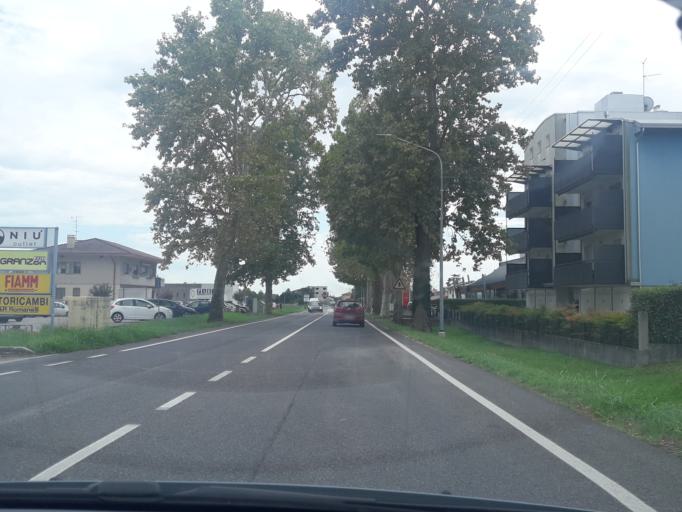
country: IT
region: Friuli Venezia Giulia
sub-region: Provincia di Udine
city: Udine
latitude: 46.0268
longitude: 13.2592
